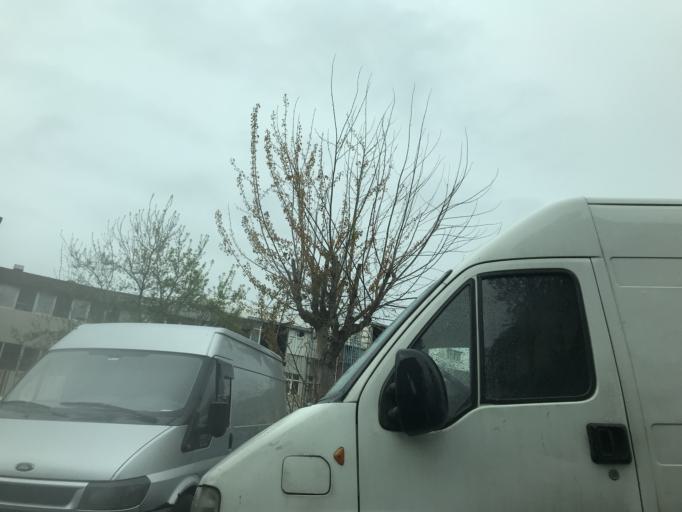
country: TR
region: Istanbul
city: merter keresteciler
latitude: 41.0210
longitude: 28.8837
